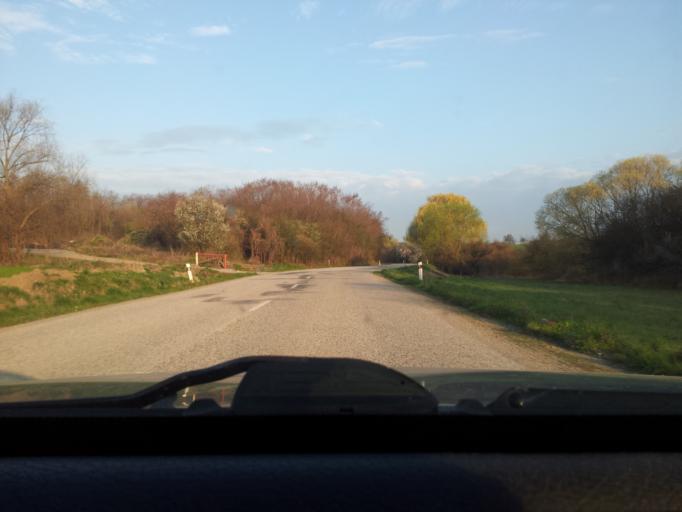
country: SK
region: Nitriansky
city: Tlmace
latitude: 48.2800
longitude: 18.4811
